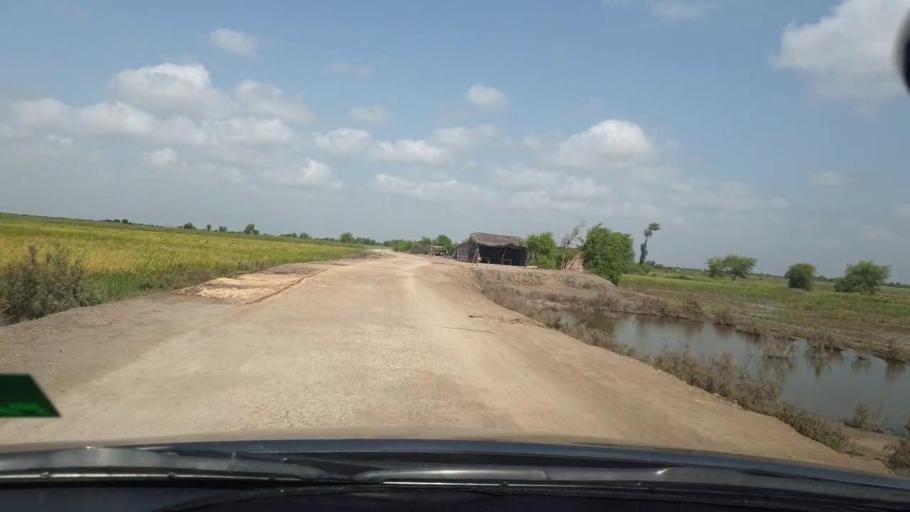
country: PK
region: Sindh
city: Tando Bago
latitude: 24.8546
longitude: 69.0602
